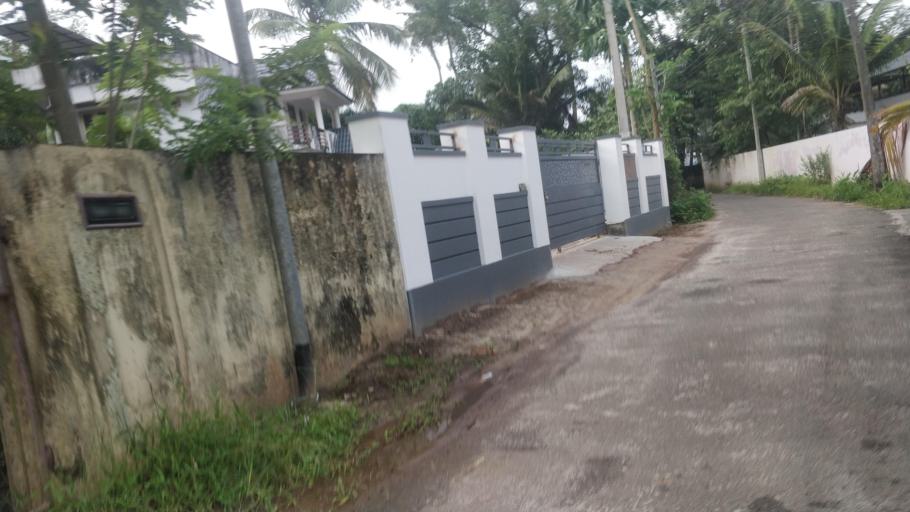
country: IN
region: Kerala
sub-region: Alappuzha
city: Shertallai
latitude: 9.6773
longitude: 76.3485
